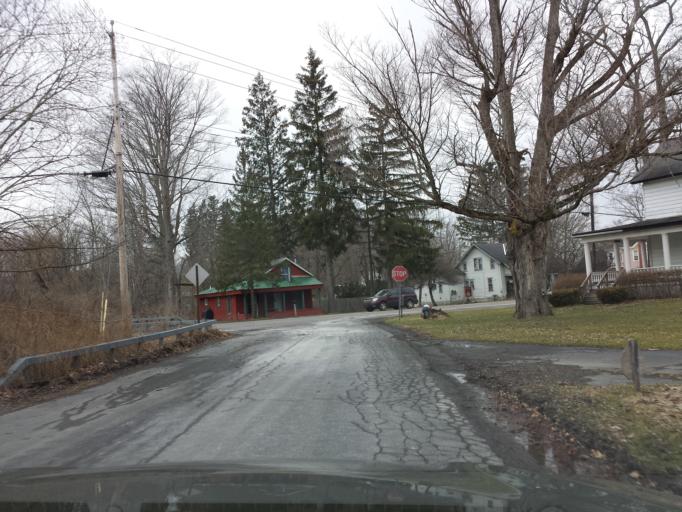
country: US
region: New York
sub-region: Tompkins County
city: Dryden
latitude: 42.3934
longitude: -76.3431
